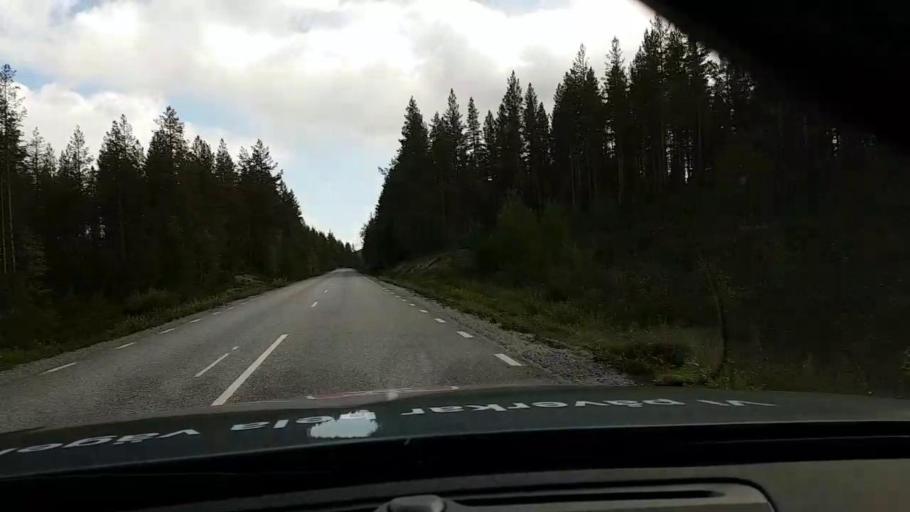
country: SE
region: Vaesternorrland
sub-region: OErnskoeldsviks Kommun
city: Bredbyn
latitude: 63.6939
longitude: 17.7664
